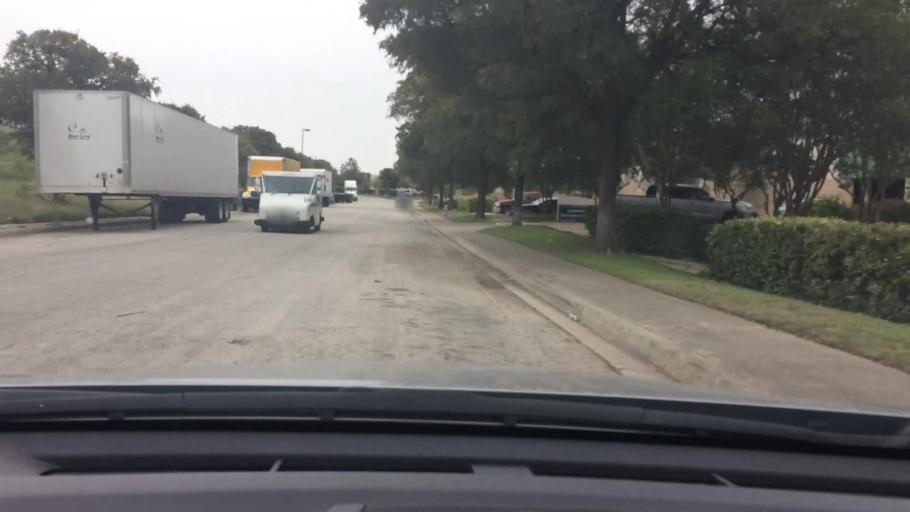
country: US
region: Texas
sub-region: Bexar County
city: Windcrest
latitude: 29.5417
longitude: -98.3722
